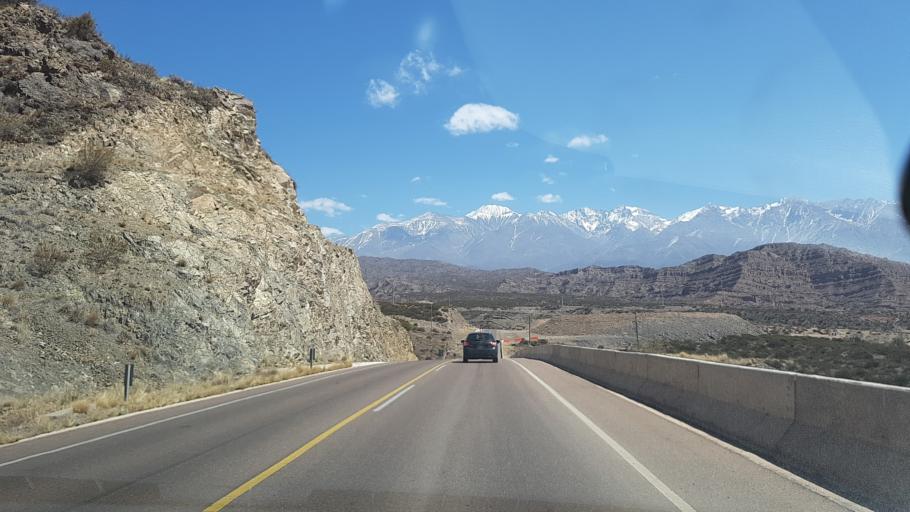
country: AR
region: Mendoza
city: Lujan de Cuyo
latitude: -32.9922
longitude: -69.1576
